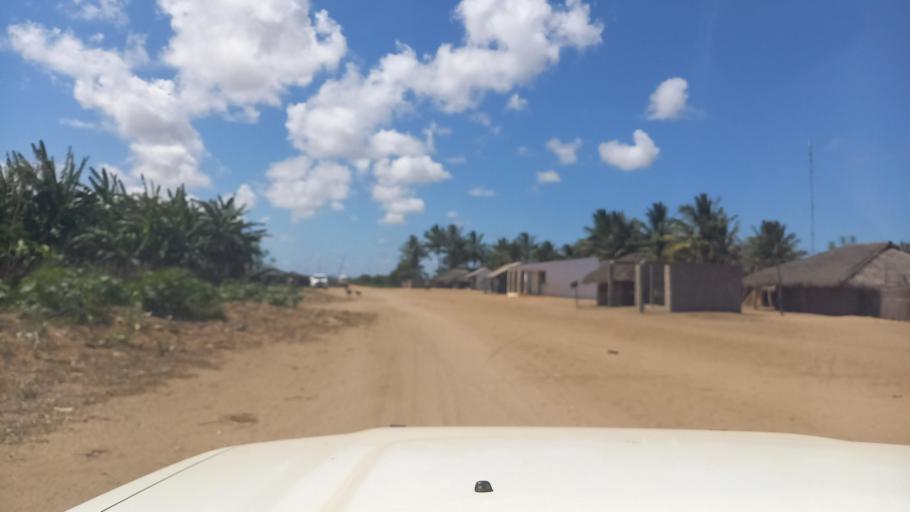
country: MZ
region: Cabo Delgado
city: Pemba
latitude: -13.4170
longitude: 40.5210
